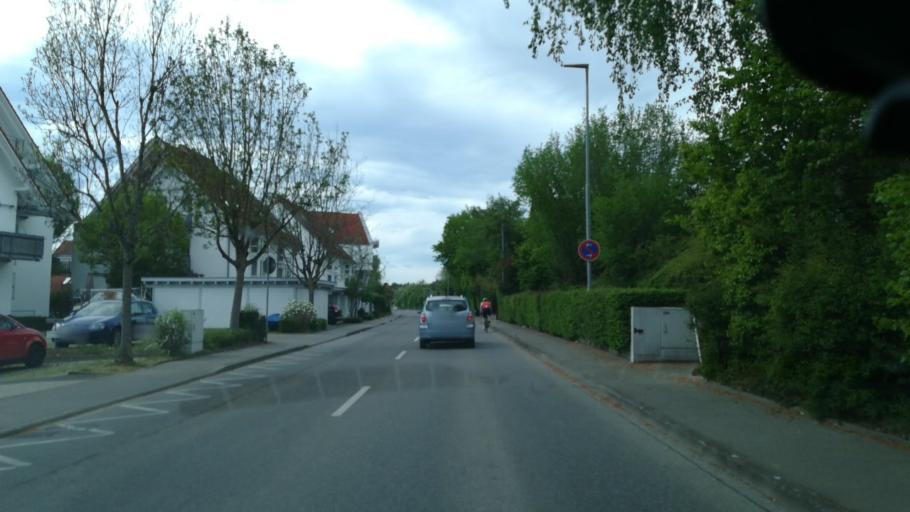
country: DE
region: Baden-Wuerttemberg
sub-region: Freiburg Region
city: Radolfzell am Bodensee
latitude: 47.7435
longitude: 9.0019
